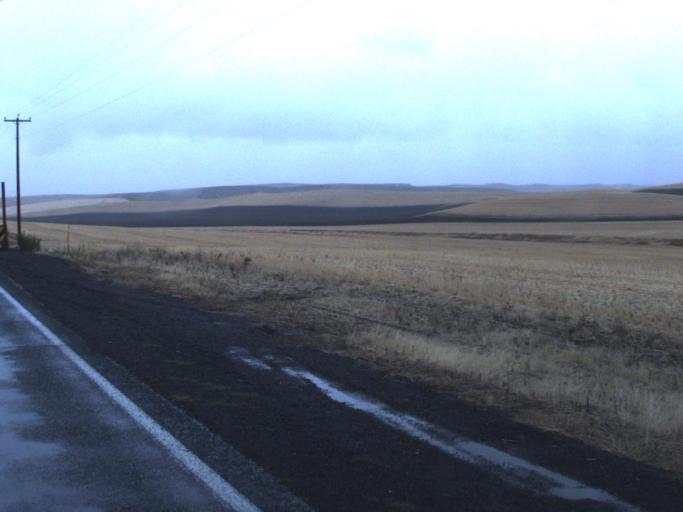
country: US
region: Washington
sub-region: Whitman County
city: Colfax
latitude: 47.0054
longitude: -117.4511
